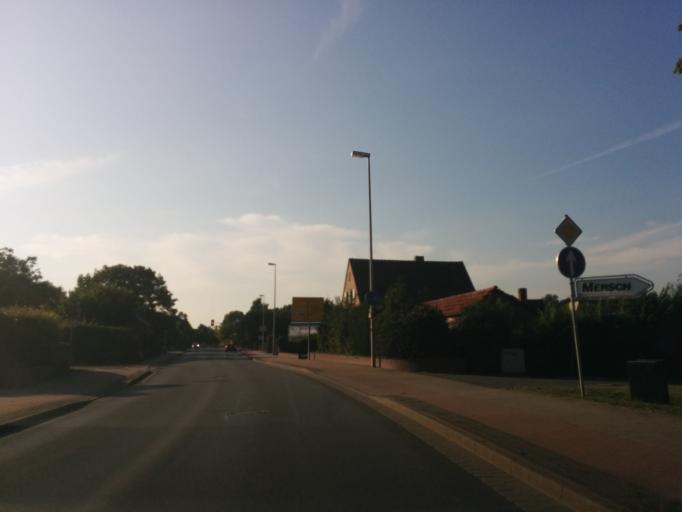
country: DE
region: North Rhine-Westphalia
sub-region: Regierungsbezirk Munster
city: Neuenkirchen
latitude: 52.2431
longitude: 7.3809
